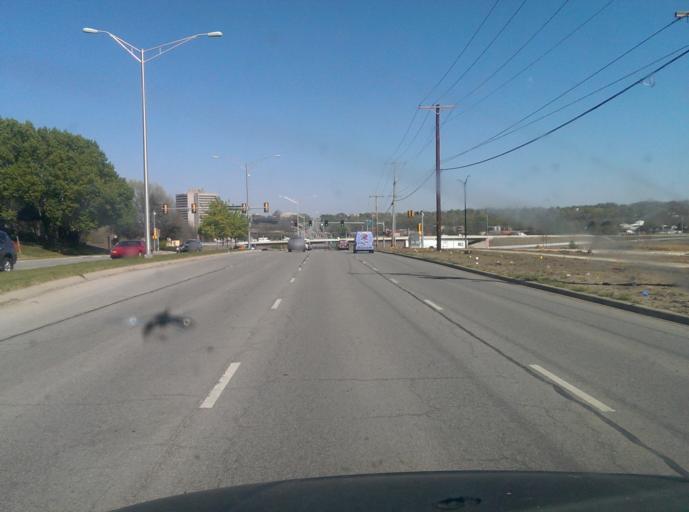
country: US
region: Kansas
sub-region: Johnson County
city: Lenexa
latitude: 38.9274
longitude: -94.7107
